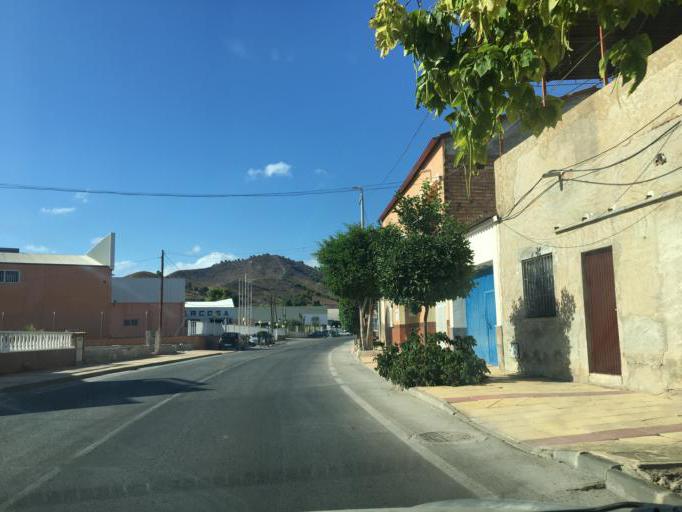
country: ES
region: Murcia
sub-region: Murcia
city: Murcia
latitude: 38.0238
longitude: -1.0896
